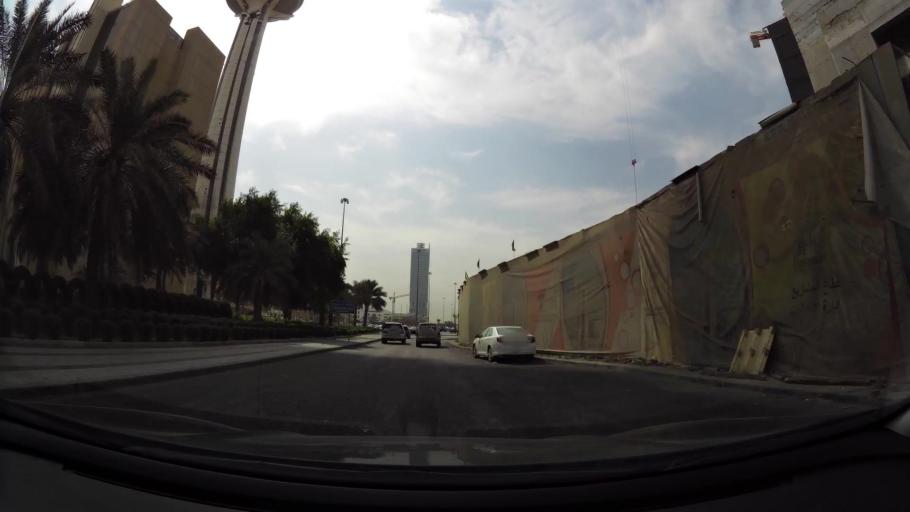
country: KW
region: Al Asimah
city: Kuwait City
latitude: 29.3694
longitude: 47.9738
